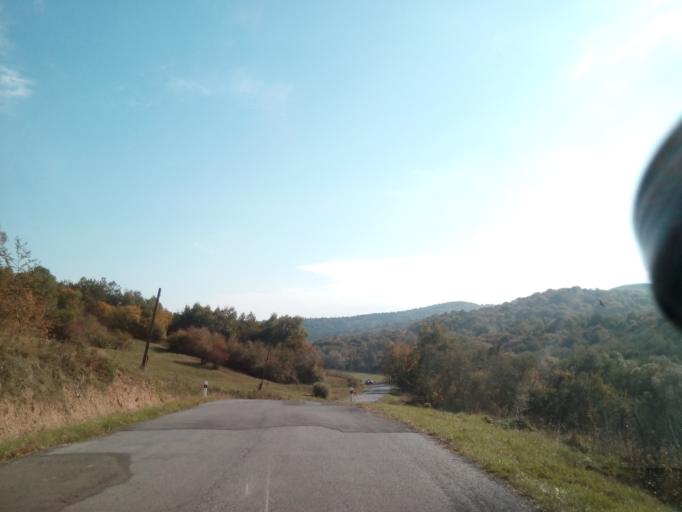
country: SK
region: Presovsky
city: Svidnik
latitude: 49.3558
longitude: 21.4465
